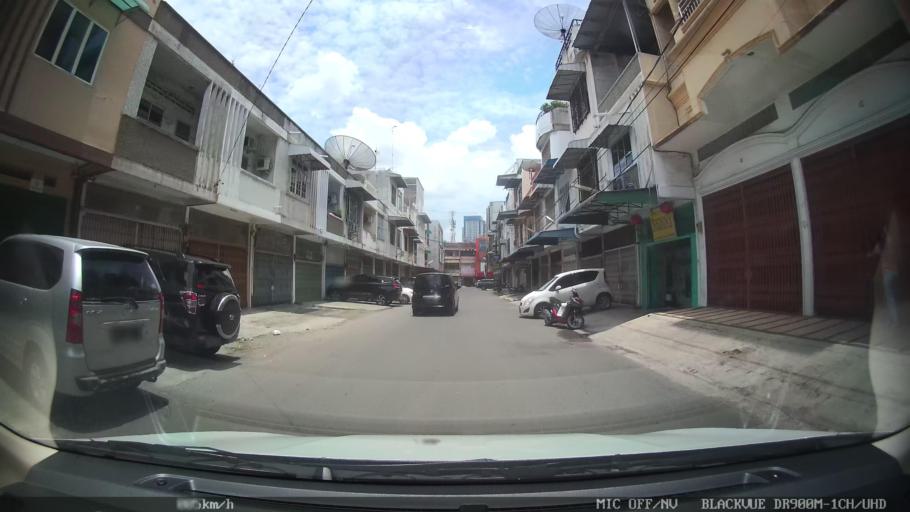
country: ID
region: North Sumatra
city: Medan
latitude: 3.5919
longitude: 98.6664
